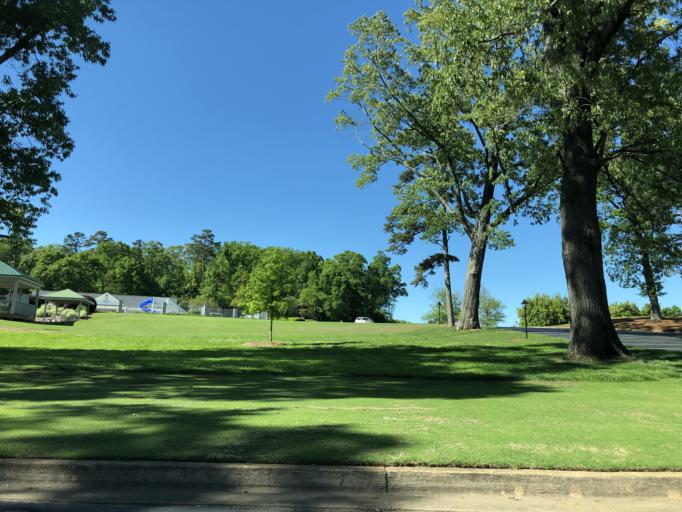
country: US
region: Georgia
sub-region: Clarke County
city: Country Club Estates
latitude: 33.9770
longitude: -83.4132
